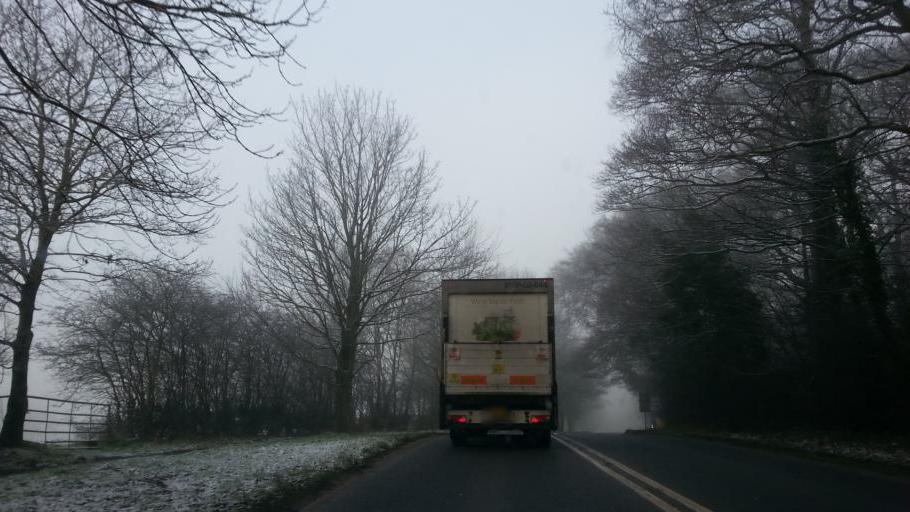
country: GB
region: England
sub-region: Cheshire East
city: Eaton
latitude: 53.1829
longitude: -2.2102
